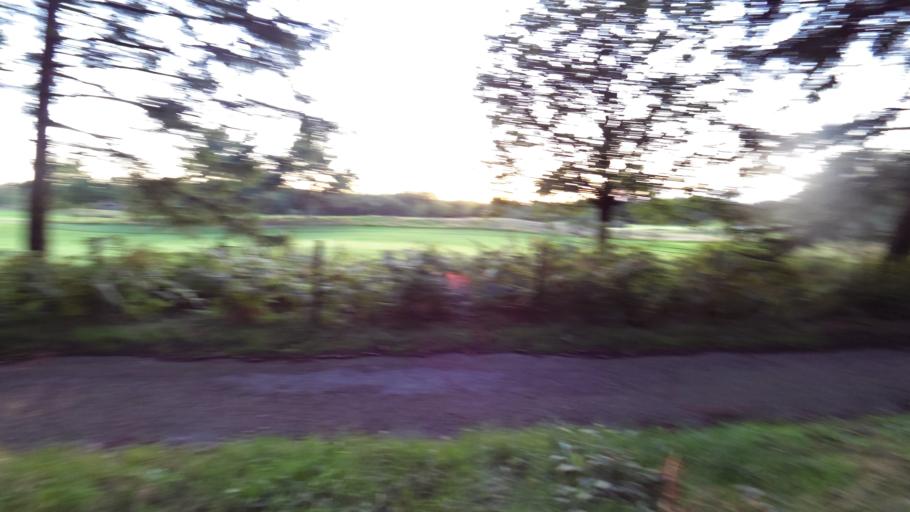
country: NL
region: Utrecht
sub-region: Gemeente Soest
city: Soest
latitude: 52.1592
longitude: 5.2401
